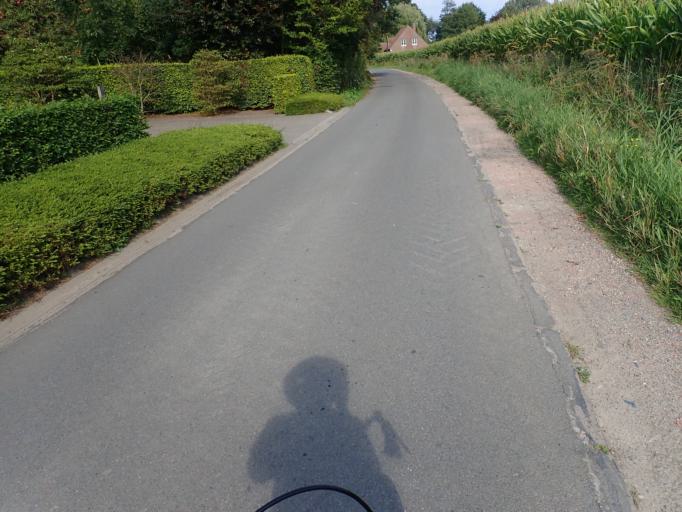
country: BE
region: Flanders
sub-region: Provincie Antwerpen
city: Sint-Amands
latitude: 51.0646
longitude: 4.2287
